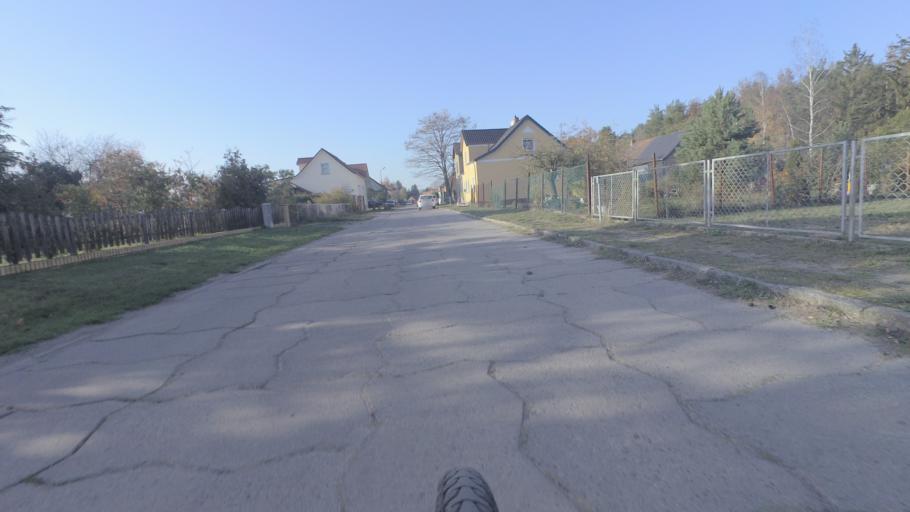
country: DE
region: Brandenburg
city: Sperenberg
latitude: 52.1691
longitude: 13.3698
